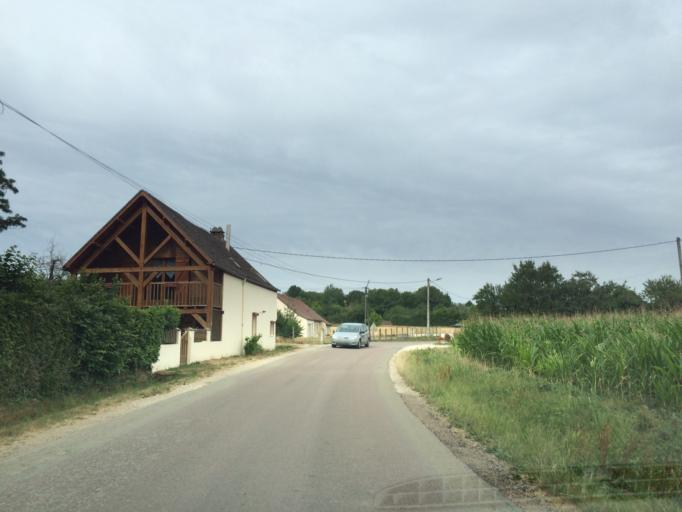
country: FR
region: Bourgogne
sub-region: Departement de l'Yonne
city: Aillant-sur-Tholon
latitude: 47.8521
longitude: 3.3540
